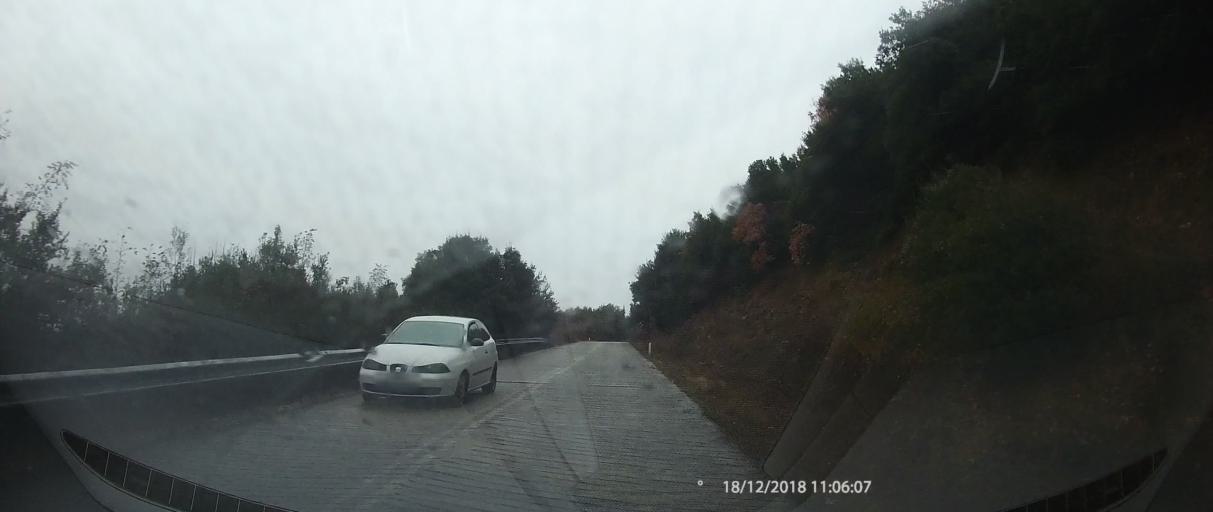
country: GR
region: Central Macedonia
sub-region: Nomos Pierias
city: Kato Milia
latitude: 40.2183
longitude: 22.3240
